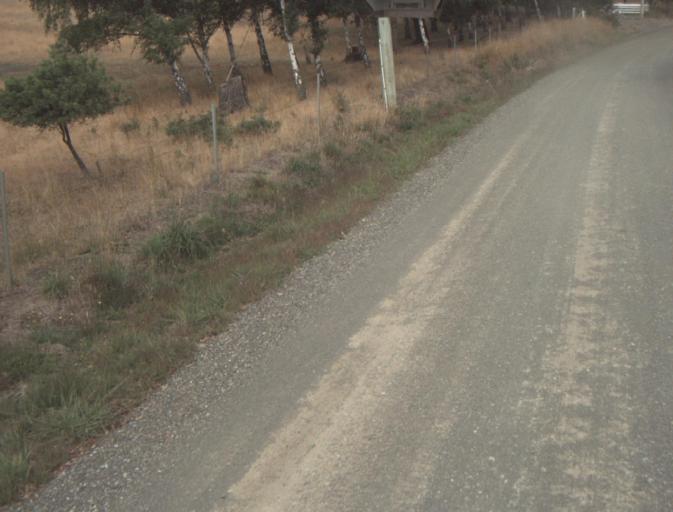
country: AU
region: Tasmania
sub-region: Launceston
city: Mayfield
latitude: -41.2195
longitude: 147.1479
